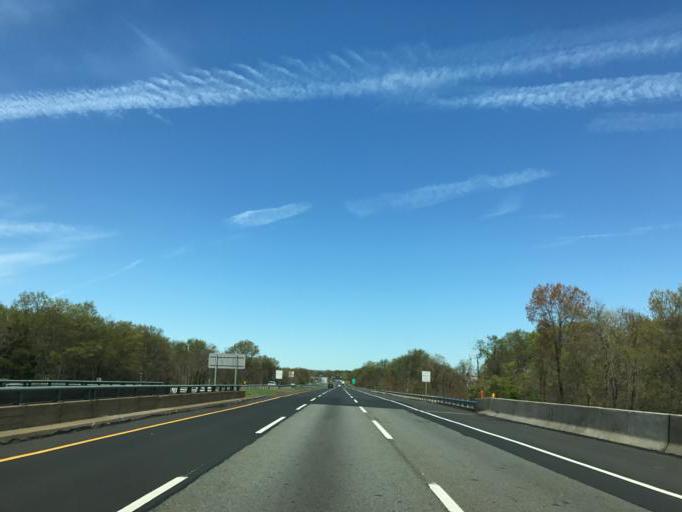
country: US
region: New Jersey
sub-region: Burlington County
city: Roebling
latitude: 40.1046
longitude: -74.7956
